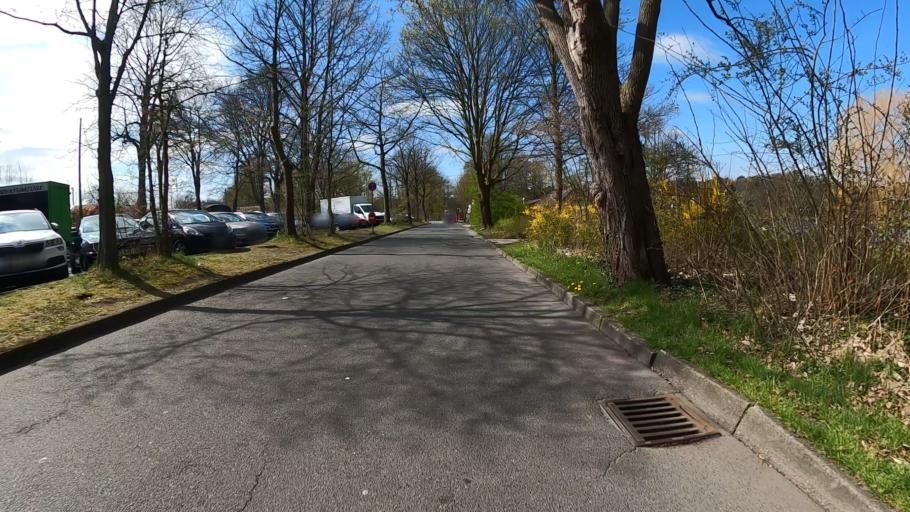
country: DE
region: Hamburg
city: Harburg
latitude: 53.4483
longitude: 9.9825
